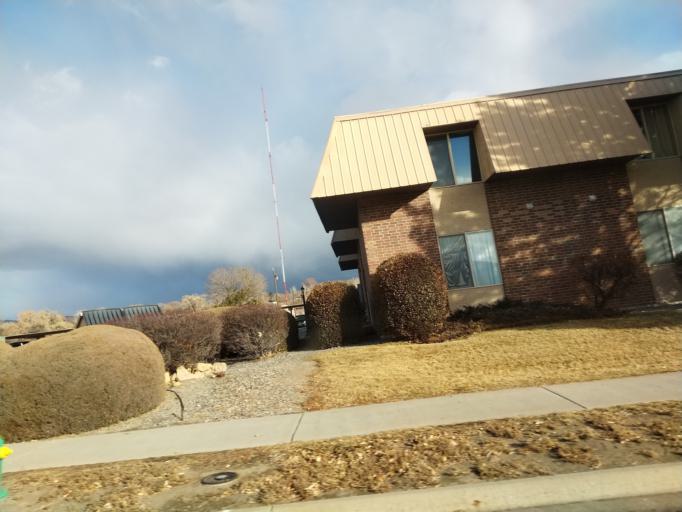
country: US
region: Colorado
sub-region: Mesa County
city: Grand Junction
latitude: 39.0946
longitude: -108.5802
